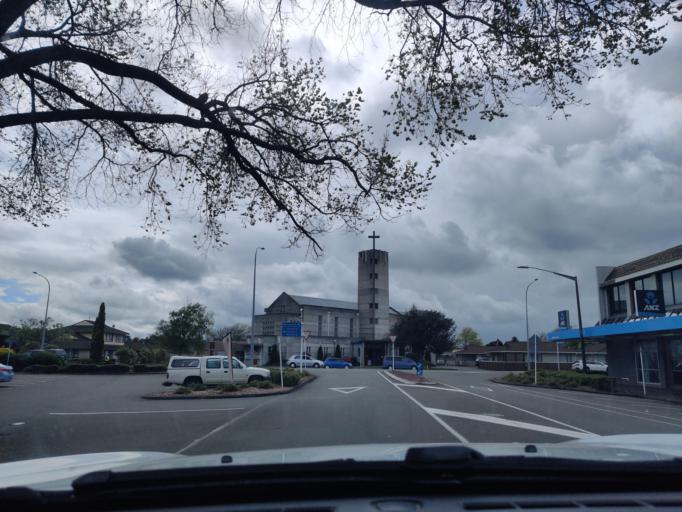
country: NZ
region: Manawatu-Wanganui
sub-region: Palmerston North City
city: Palmerston North
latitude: -40.3476
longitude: 175.6273
